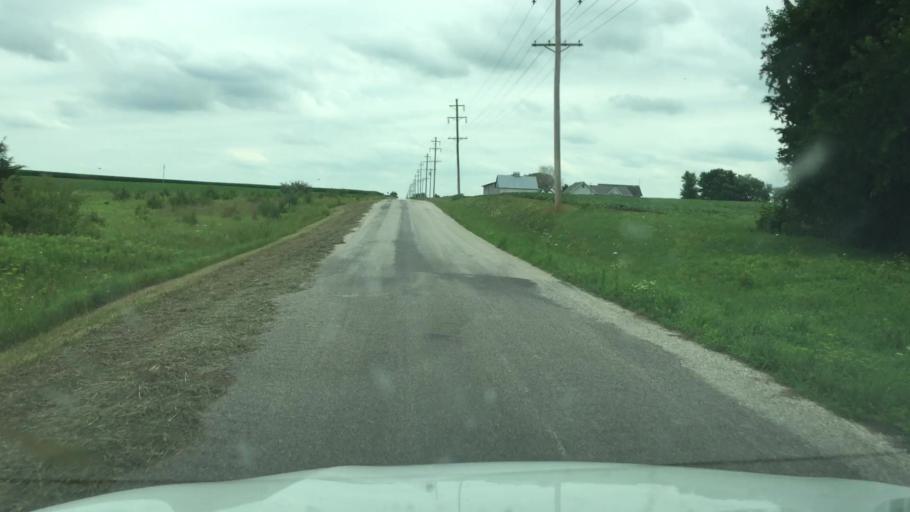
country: US
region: Illinois
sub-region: Hancock County
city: Carthage
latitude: 40.3452
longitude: -91.0822
